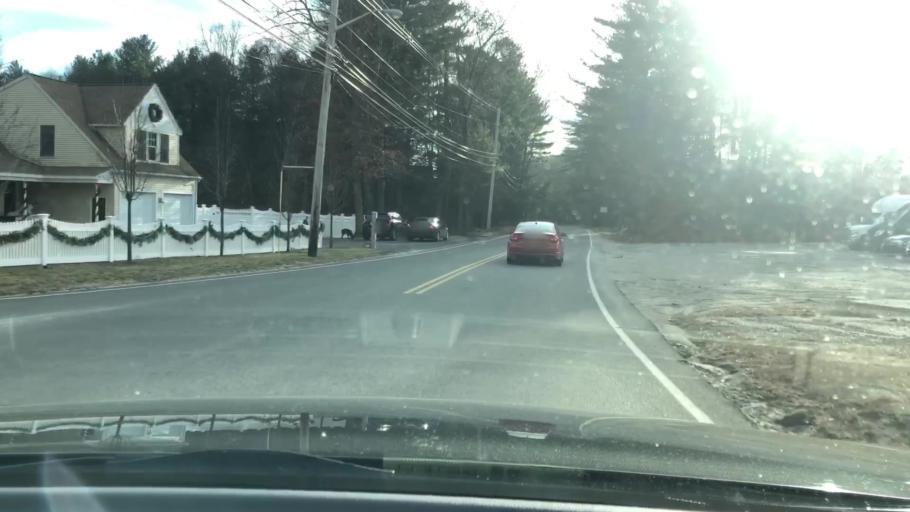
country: US
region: Massachusetts
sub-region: Worcester County
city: Milford
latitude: 42.1098
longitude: -71.5135
